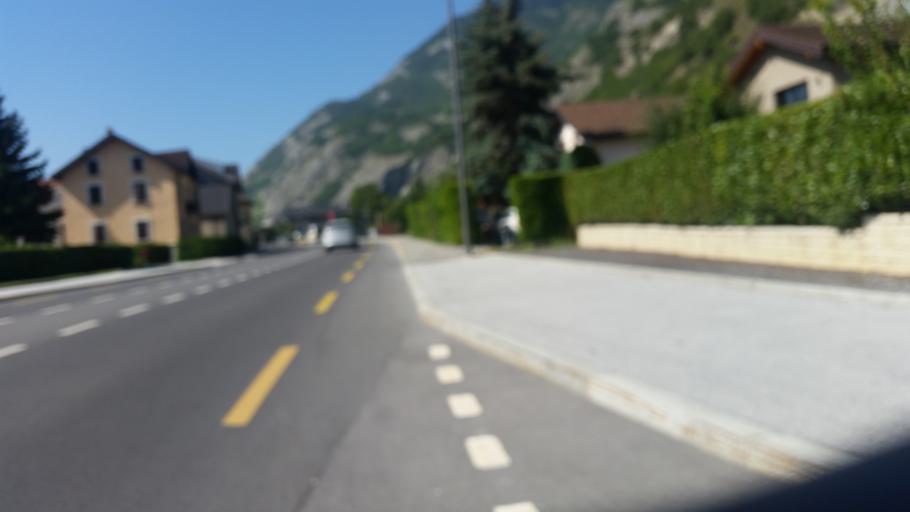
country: CH
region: Valais
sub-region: Conthey District
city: Ardon
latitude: 46.2216
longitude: 7.2689
